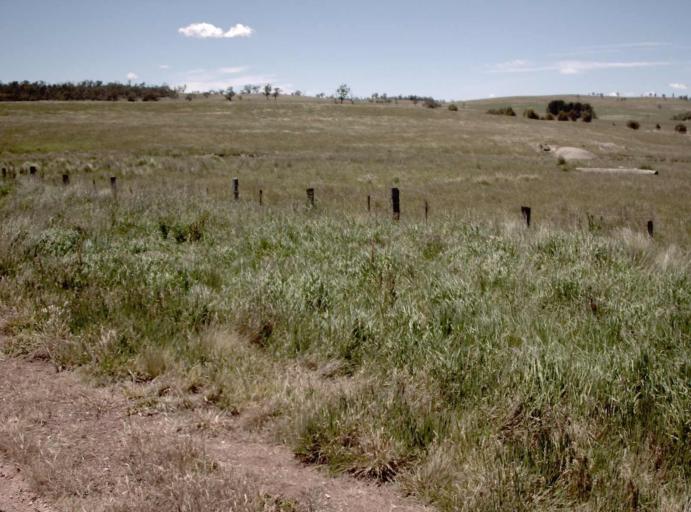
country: AU
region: New South Wales
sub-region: Snowy River
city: Jindabyne
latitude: -37.0134
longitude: 148.2810
